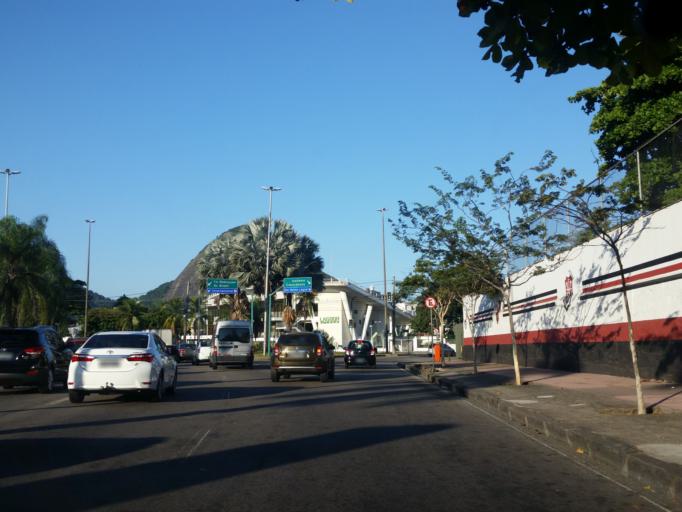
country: BR
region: Rio de Janeiro
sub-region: Rio De Janeiro
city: Rio de Janeiro
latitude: -22.9773
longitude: -43.2199
